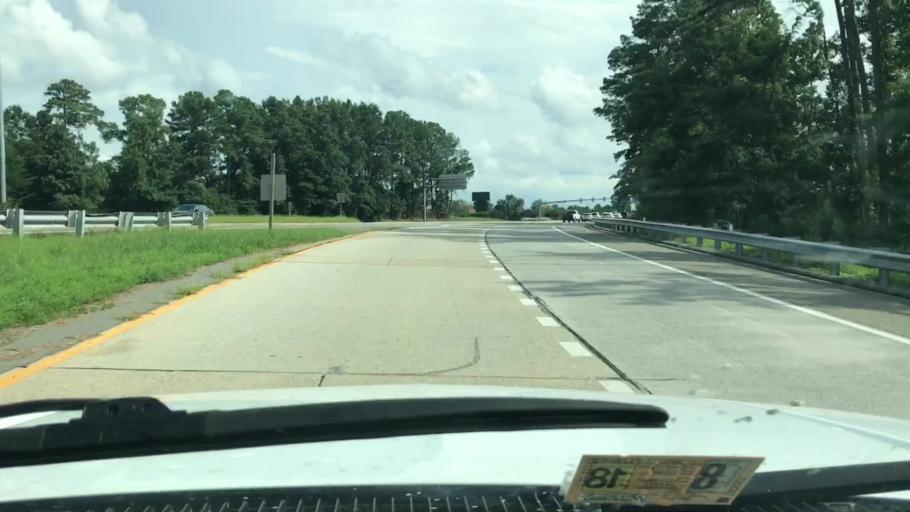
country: US
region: Virginia
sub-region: Henrico County
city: Dumbarton
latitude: 37.6043
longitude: -77.5158
